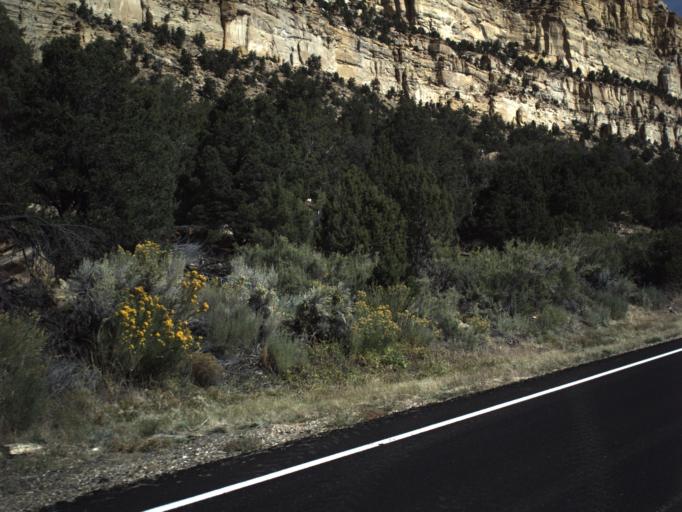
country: US
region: Utah
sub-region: Wayne County
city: Loa
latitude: 37.7306
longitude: -111.7594
